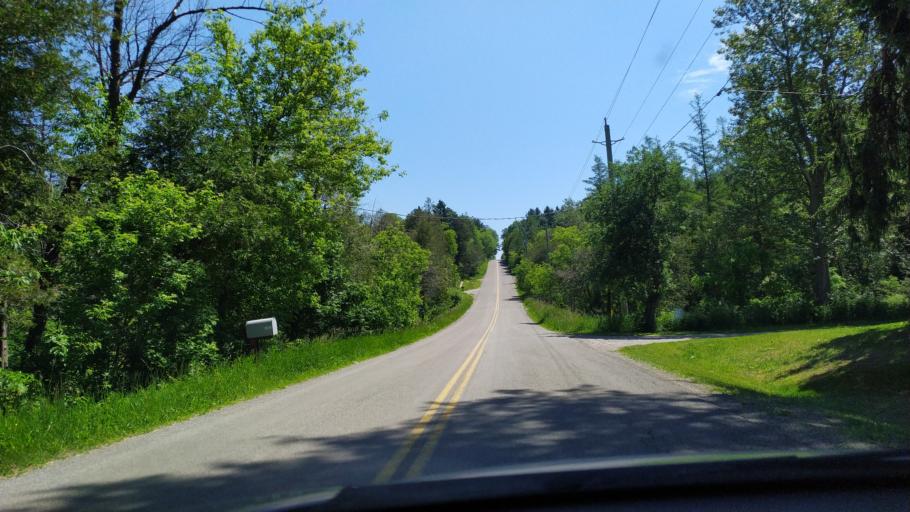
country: CA
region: Ontario
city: Waterloo
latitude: 43.4719
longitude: -80.6321
